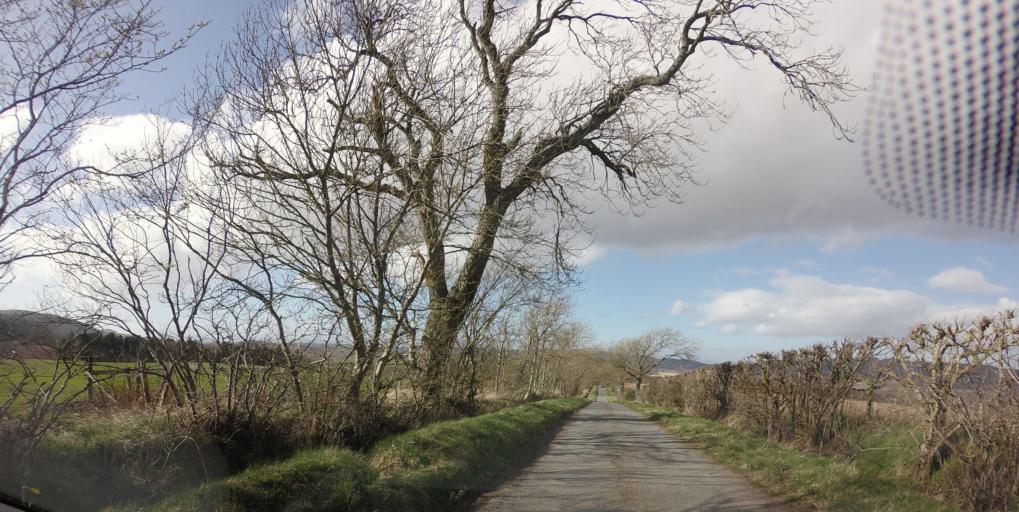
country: GB
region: Scotland
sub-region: Perth and Kinross
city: Bridge of Earn
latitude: 56.3274
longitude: -3.4148
